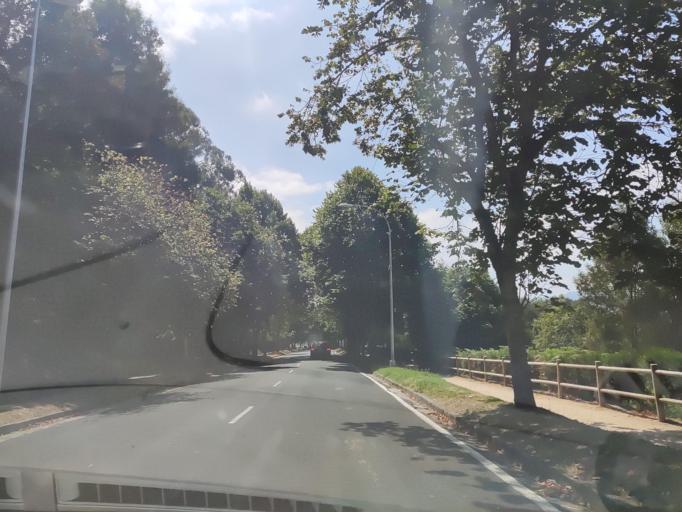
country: ES
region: Galicia
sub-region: Provincia de Pontevedra
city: Vigo
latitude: 42.2558
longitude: -8.7029
